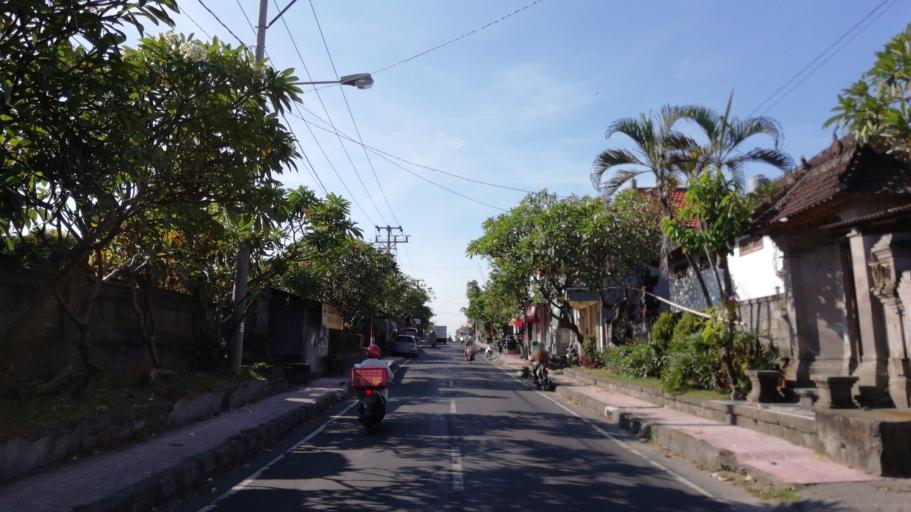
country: ID
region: Bali
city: Banjar Pasekan
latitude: -8.6304
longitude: 115.2845
